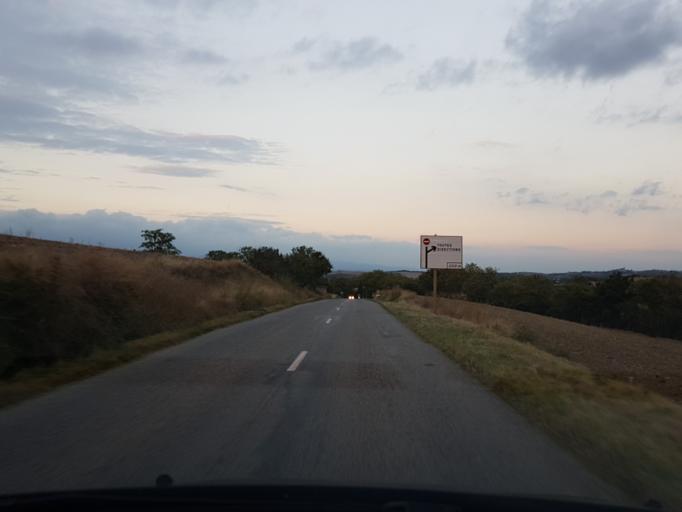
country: FR
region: Languedoc-Roussillon
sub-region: Departement de l'Aude
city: Bram
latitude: 43.1902
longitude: 2.0493
